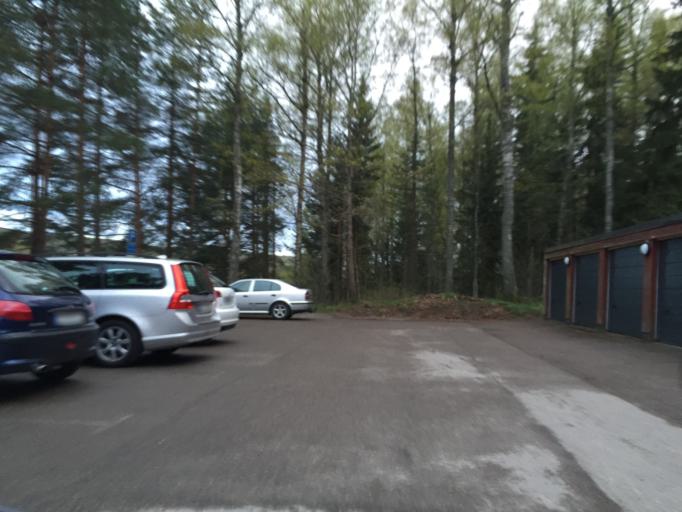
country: SE
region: Dalarna
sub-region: Ludvika Kommun
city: Ludvika
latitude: 60.1394
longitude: 15.1969
